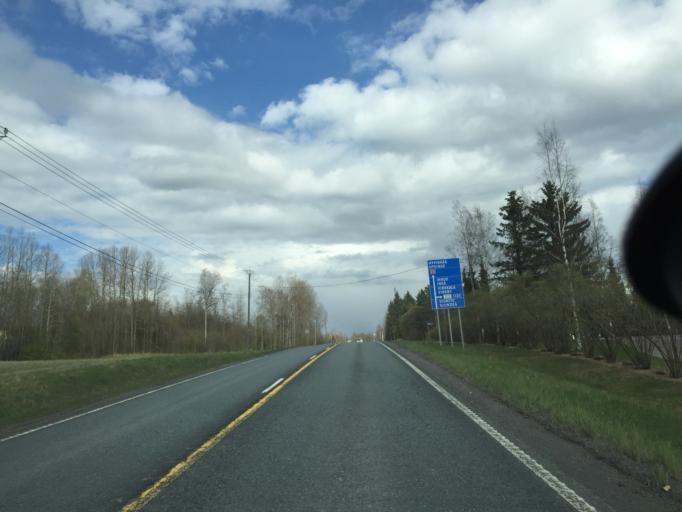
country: FI
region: Uusimaa
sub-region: Helsinki
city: Lohja
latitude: 60.1762
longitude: 23.9804
